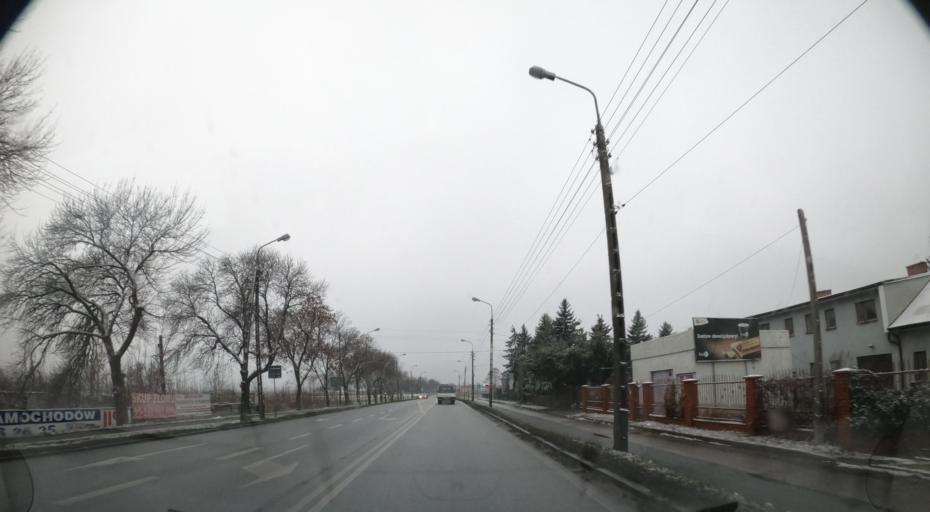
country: PL
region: Masovian Voivodeship
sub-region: Powiat warszawski zachodni
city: Blonie
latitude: 52.1991
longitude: 20.6054
